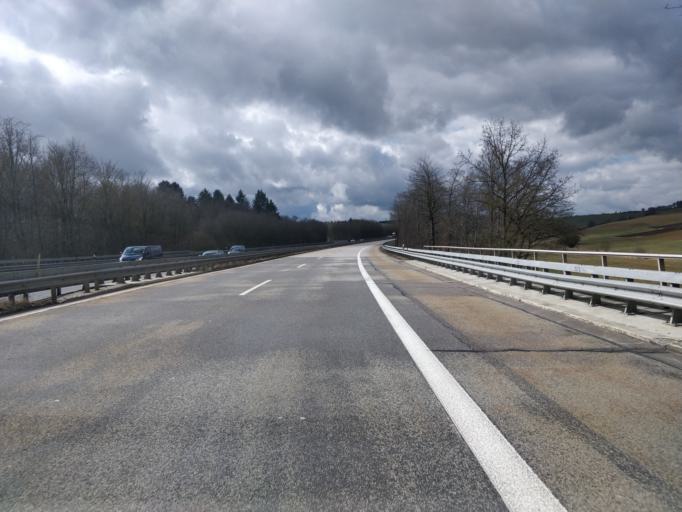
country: DE
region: Rheinland-Pfalz
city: Udler
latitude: 50.1432
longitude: 6.8728
